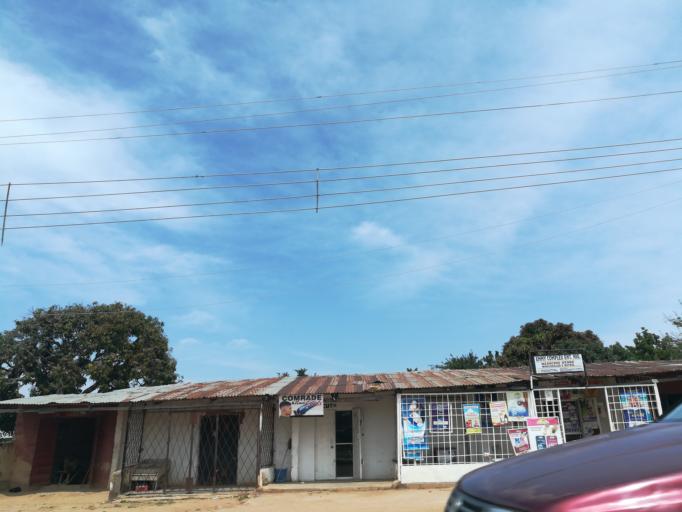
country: NG
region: Plateau
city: Jos
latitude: 9.9270
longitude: 8.8447
